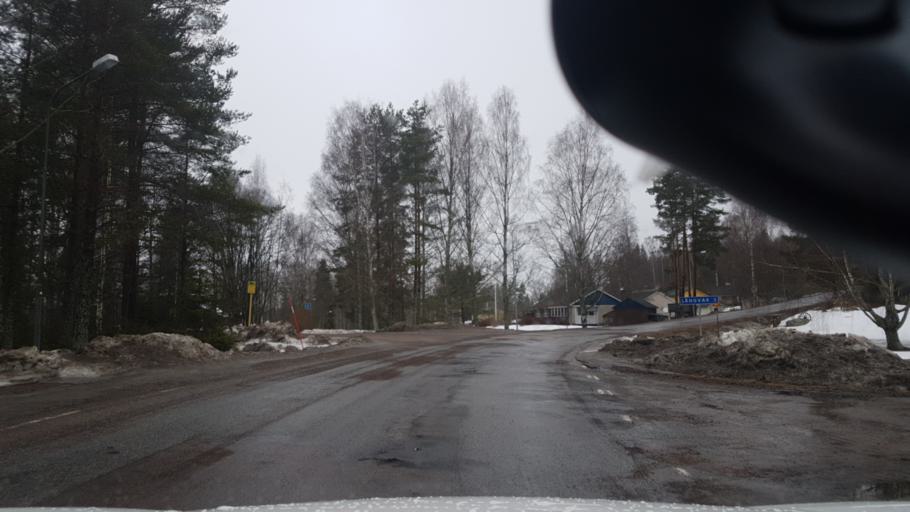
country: SE
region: Vaermland
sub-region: Arvika Kommun
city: Arvika
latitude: 59.6478
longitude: 12.7475
